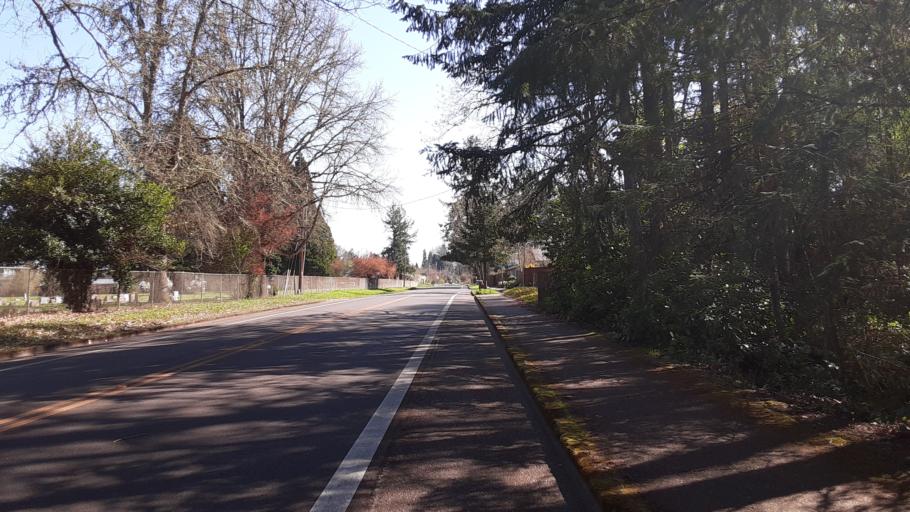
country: US
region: Oregon
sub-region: Benton County
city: Corvallis
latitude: 44.5485
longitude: -123.2557
